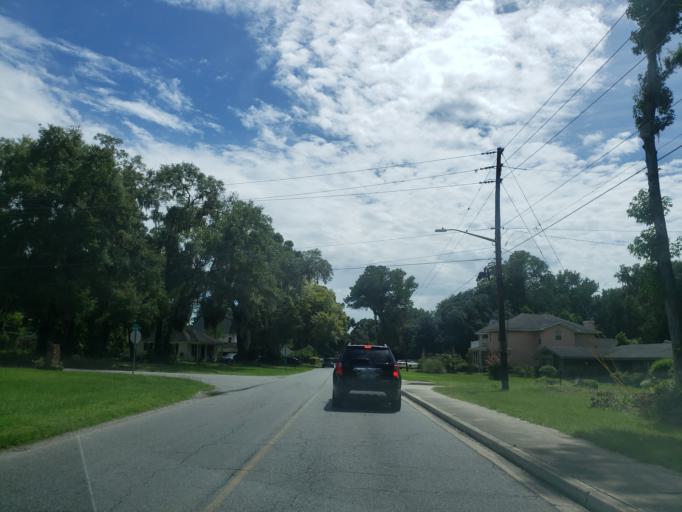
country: US
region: Georgia
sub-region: Chatham County
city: Thunderbolt
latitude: 32.0292
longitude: -81.0576
